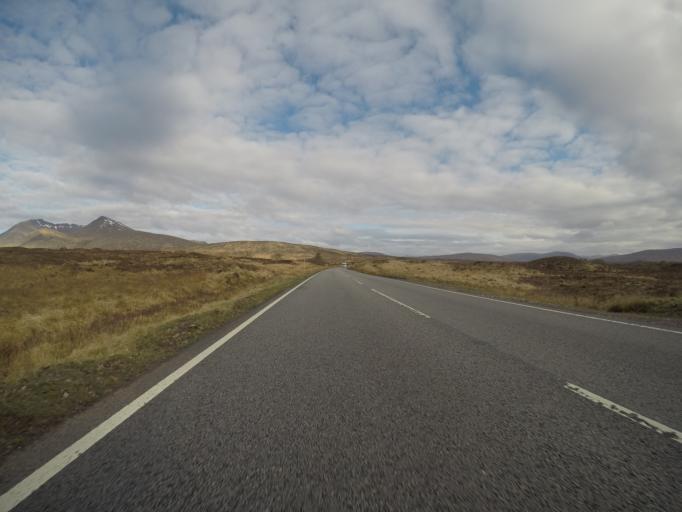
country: GB
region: Scotland
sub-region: Highland
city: Spean Bridge
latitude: 56.6027
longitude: -4.7521
